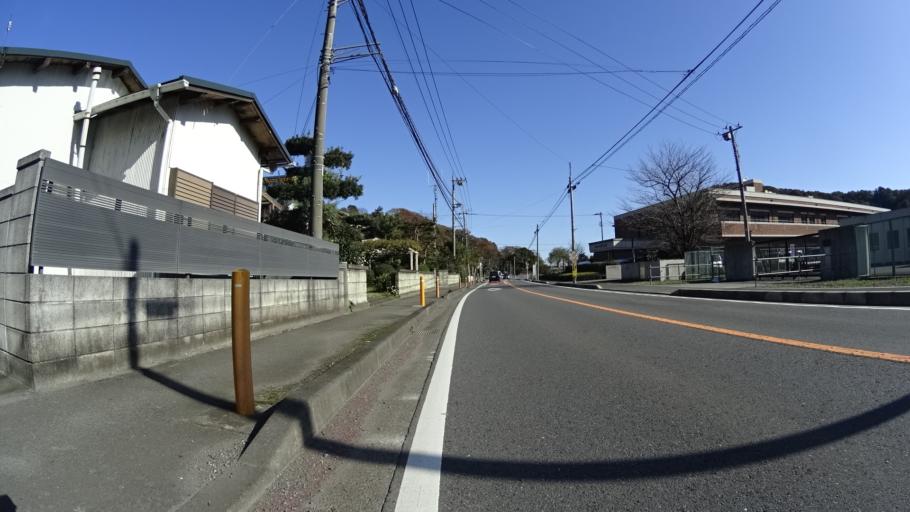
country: JP
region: Kanagawa
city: Zama
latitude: 35.5277
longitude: 139.2979
